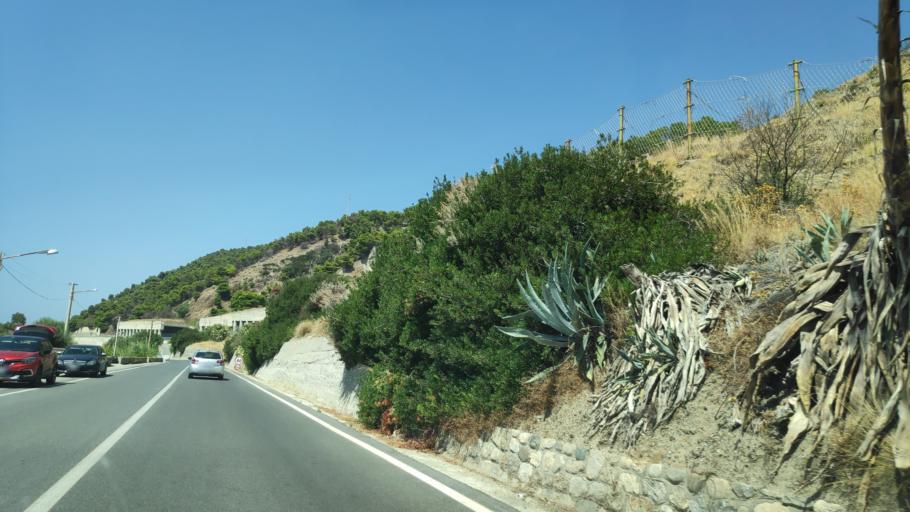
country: IT
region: Calabria
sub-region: Provincia di Reggio Calabria
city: Palizzi Marina
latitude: 37.9202
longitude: 15.9746
